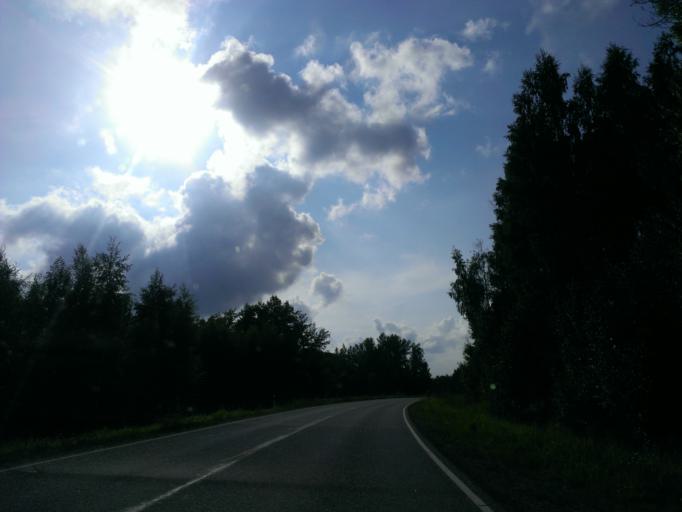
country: LV
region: Priekuli
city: Priekuli
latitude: 57.2934
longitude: 25.4678
